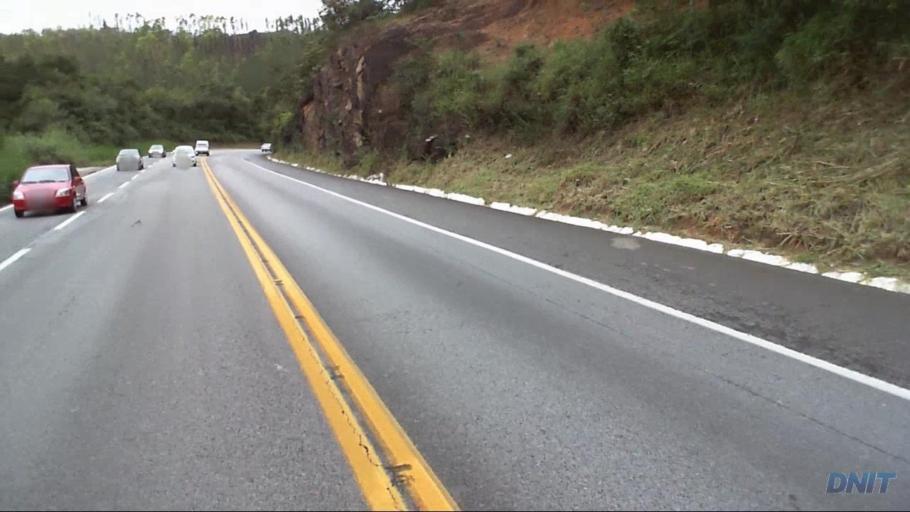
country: BR
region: Minas Gerais
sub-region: Joao Monlevade
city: Joao Monlevade
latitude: -19.8526
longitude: -43.2661
